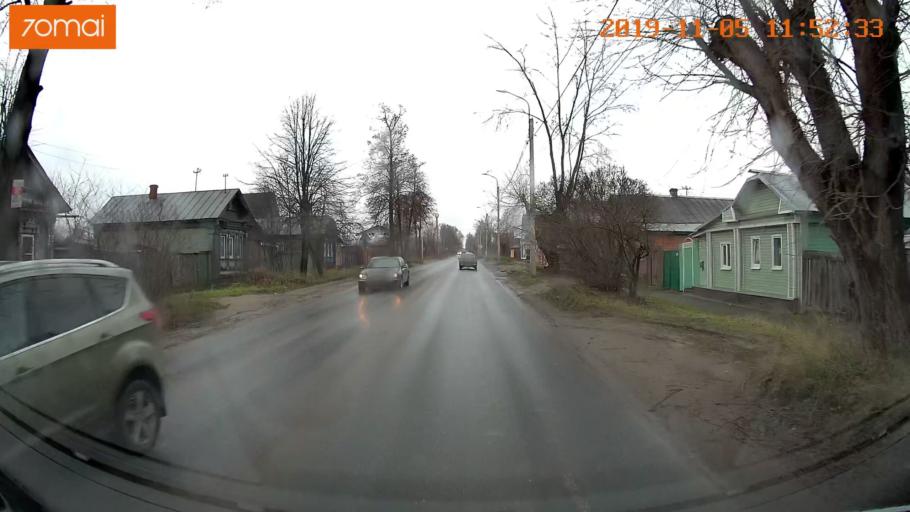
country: RU
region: Ivanovo
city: Bogorodskoye
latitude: 56.9998
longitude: 41.0295
